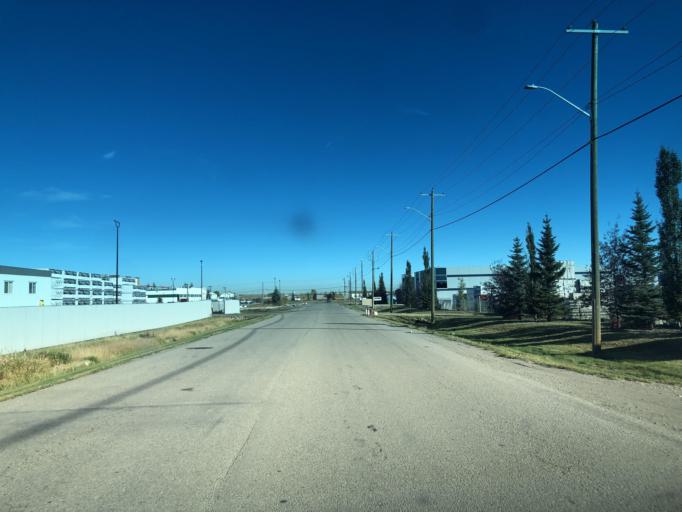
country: CA
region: Alberta
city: Chestermere
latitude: 50.9675
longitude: -113.9026
